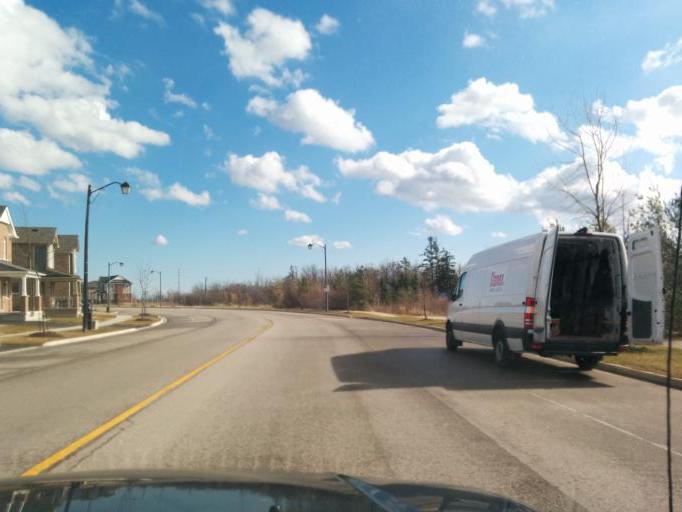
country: CA
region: Ontario
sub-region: Halton
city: Milton
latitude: 43.5021
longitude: -79.8468
